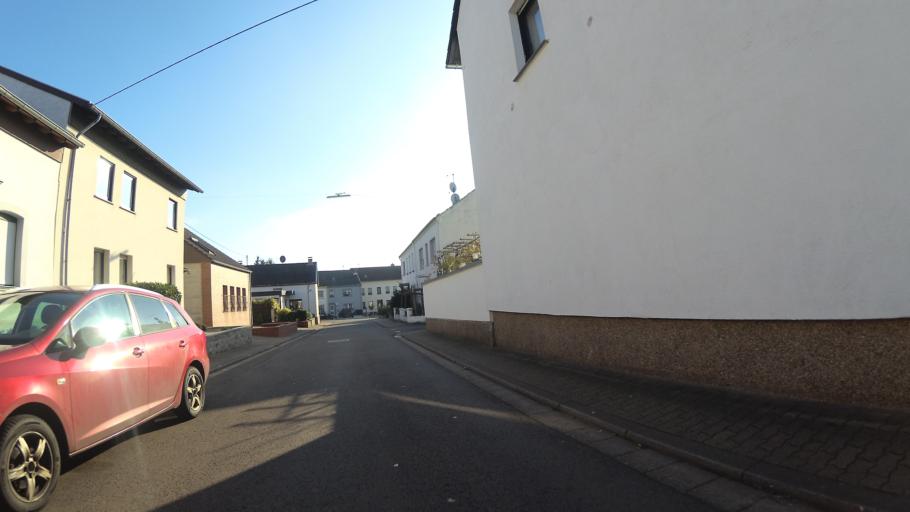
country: DE
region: Saarland
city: Ensdorf
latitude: 49.3097
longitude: 6.7747
